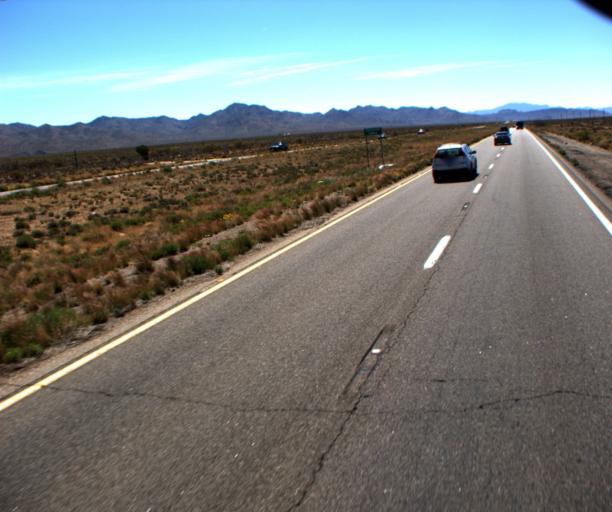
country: US
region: Arizona
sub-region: Mohave County
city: Golden Valley
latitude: 35.3349
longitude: -114.2148
